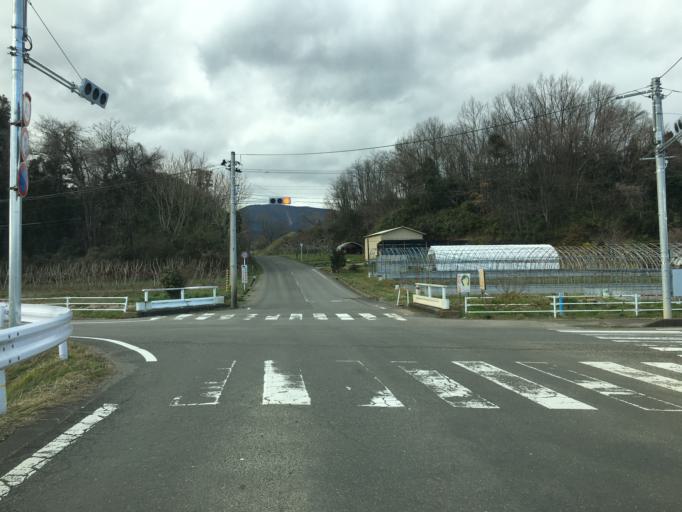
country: JP
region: Fukushima
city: Hobaramachi
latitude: 37.8486
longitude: 140.5357
